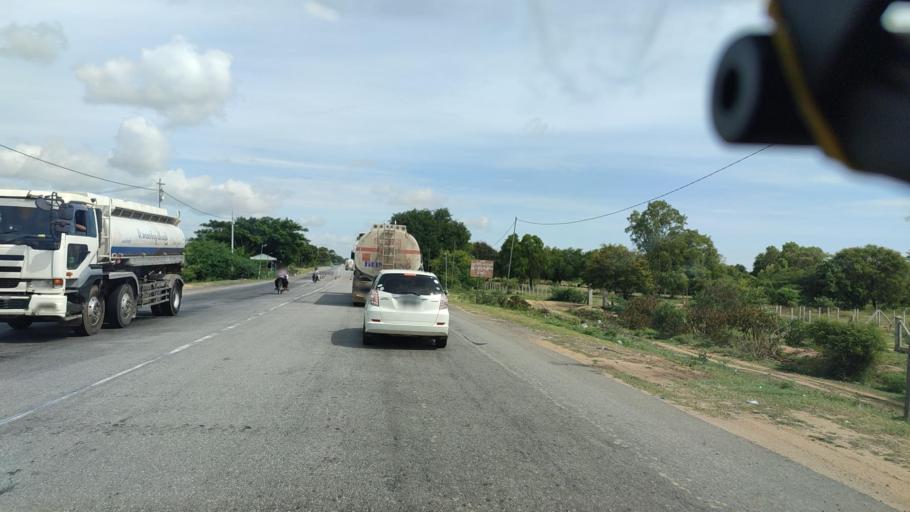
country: MM
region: Mandalay
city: Yamethin
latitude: 20.4570
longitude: 96.1238
